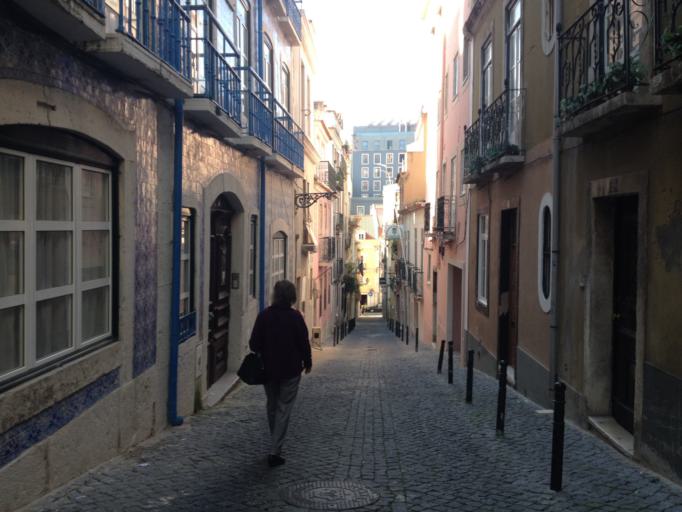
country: PT
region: Lisbon
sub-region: Lisbon
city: Lisbon
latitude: 38.7201
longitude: -9.1426
